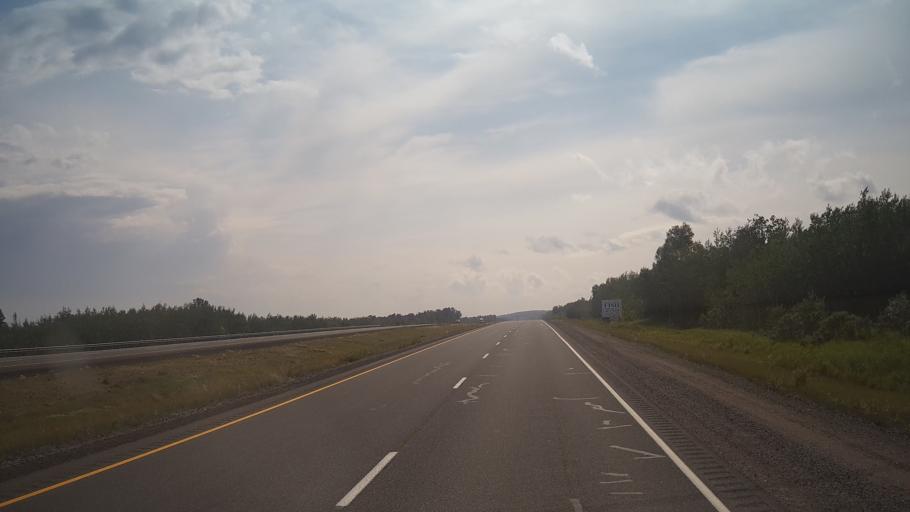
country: CA
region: Ontario
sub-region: Thunder Bay District
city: Thunder Bay
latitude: 48.5652
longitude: -88.8616
